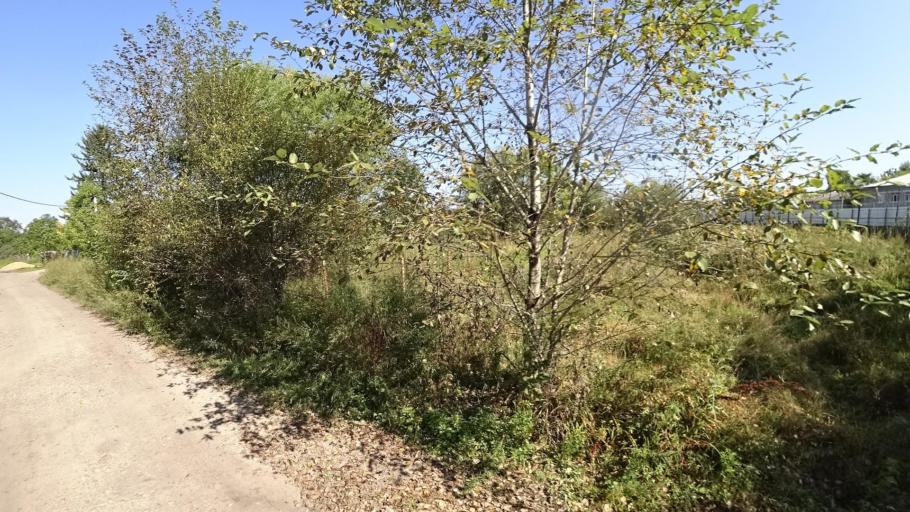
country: RU
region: Jewish Autonomous Oblast
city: Bira
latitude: 48.9903
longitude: 132.4634
